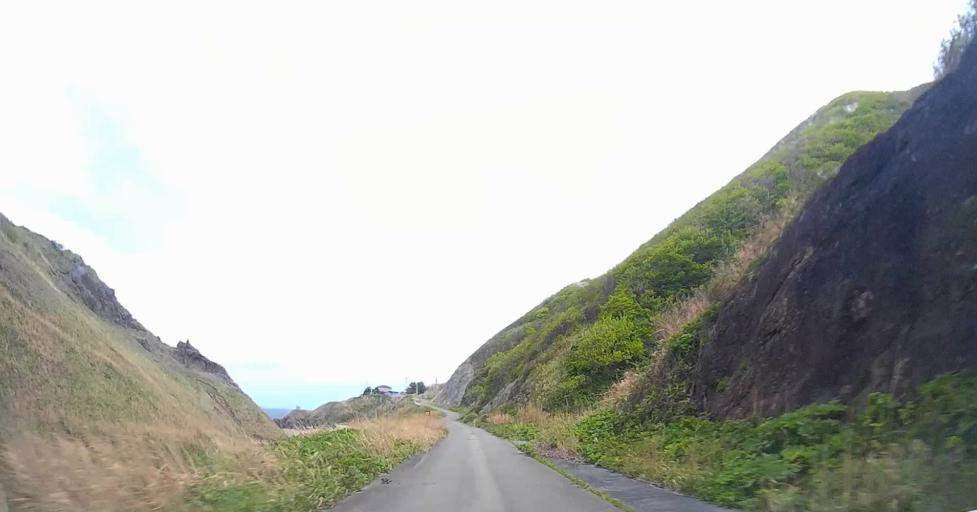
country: JP
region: Aomori
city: Shimokizukuri
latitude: 41.2408
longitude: 140.3432
